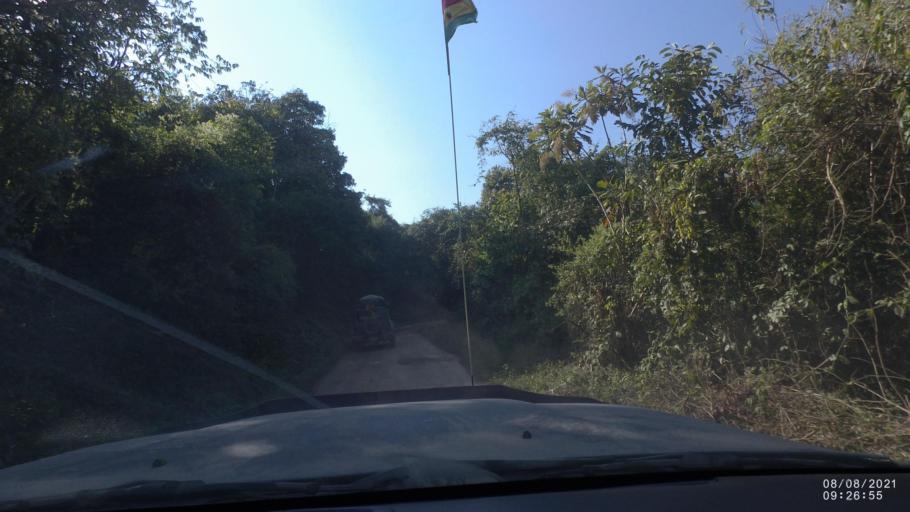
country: BO
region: La Paz
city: Quime
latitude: -16.5897
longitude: -66.7215
